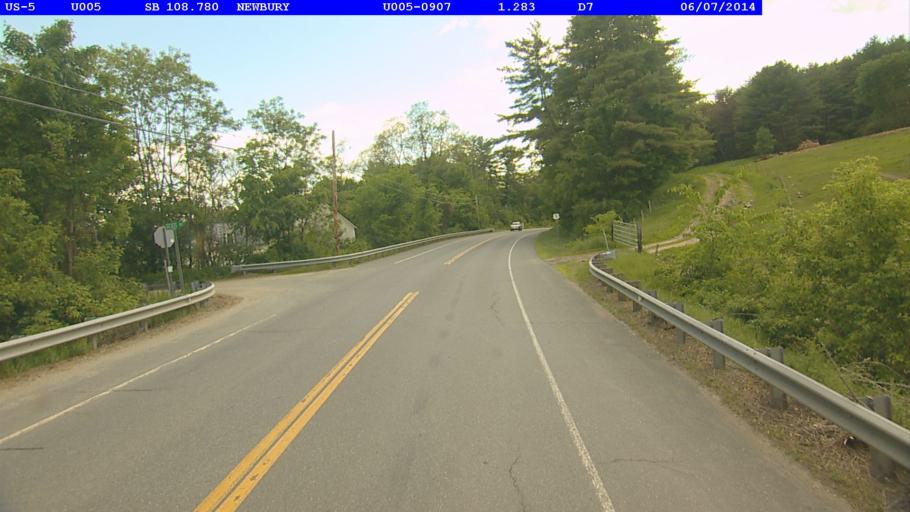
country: US
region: New Hampshire
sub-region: Grafton County
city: Haverhill
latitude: 44.0481
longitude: -72.0770
